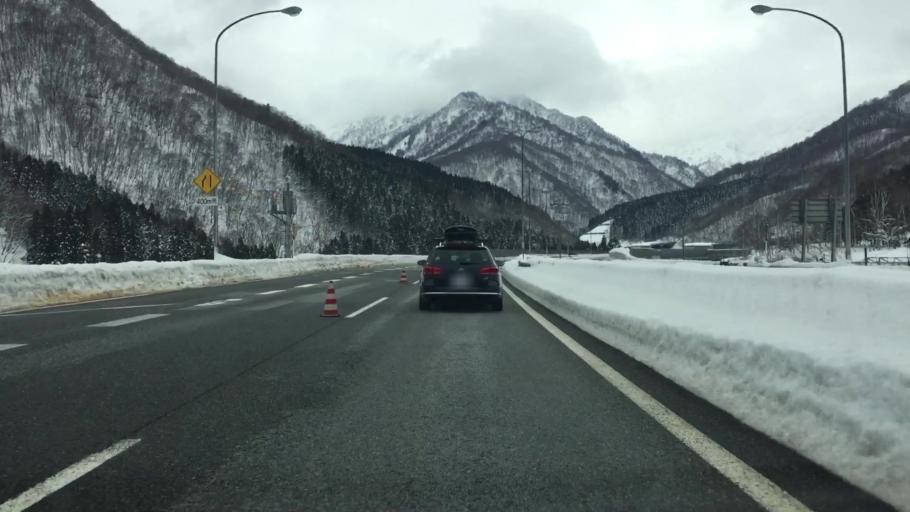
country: JP
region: Niigata
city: Shiozawa
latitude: 36.8756
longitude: 138.8620
